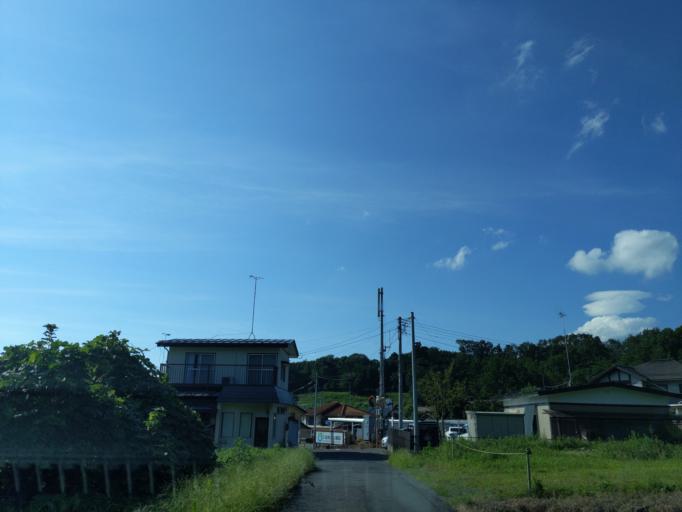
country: JP
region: Fukushima
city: Koriyama
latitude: 37.3962
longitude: 140.4241
